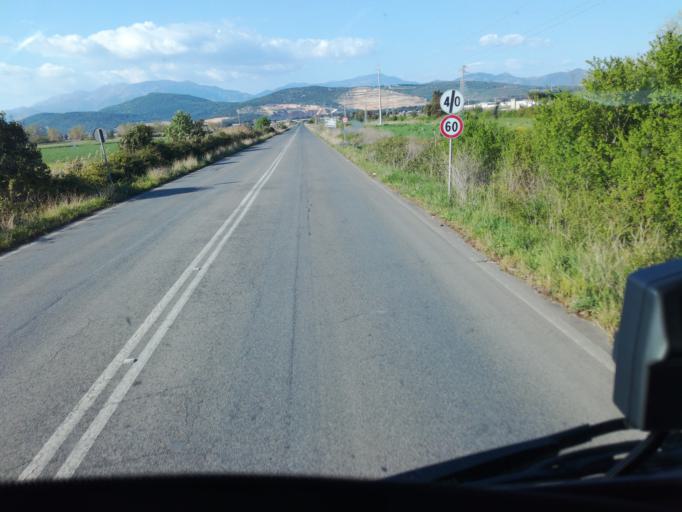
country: IT
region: Latium
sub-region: Provincia di Latina
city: Priverno
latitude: 41.4103
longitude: 13.1597
